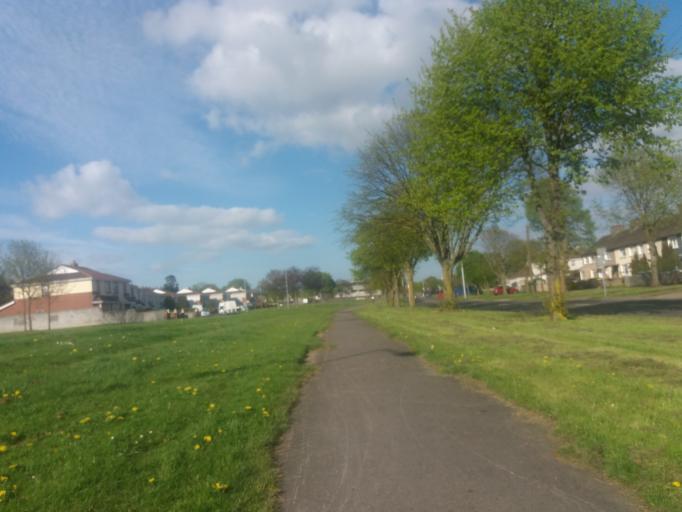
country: IE
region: Leinster
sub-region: Dublin City
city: Finglas
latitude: 53.3852
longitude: -6.3067
